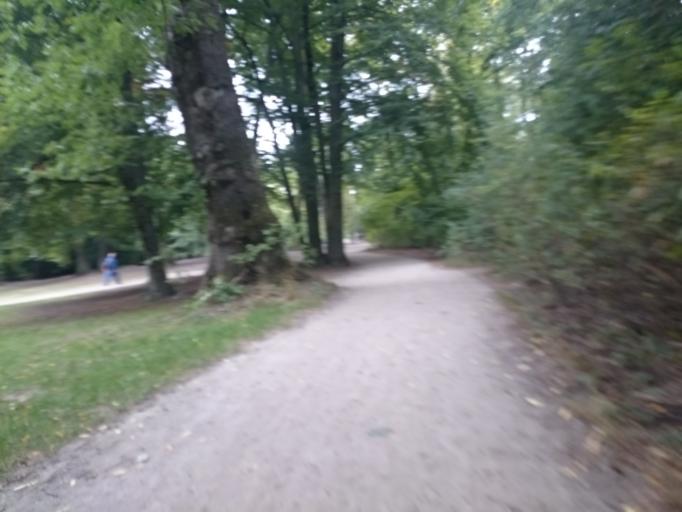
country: DE
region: Bavaria
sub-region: Upper Bavaria
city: Munich
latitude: 48.1447
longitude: 11.5884
